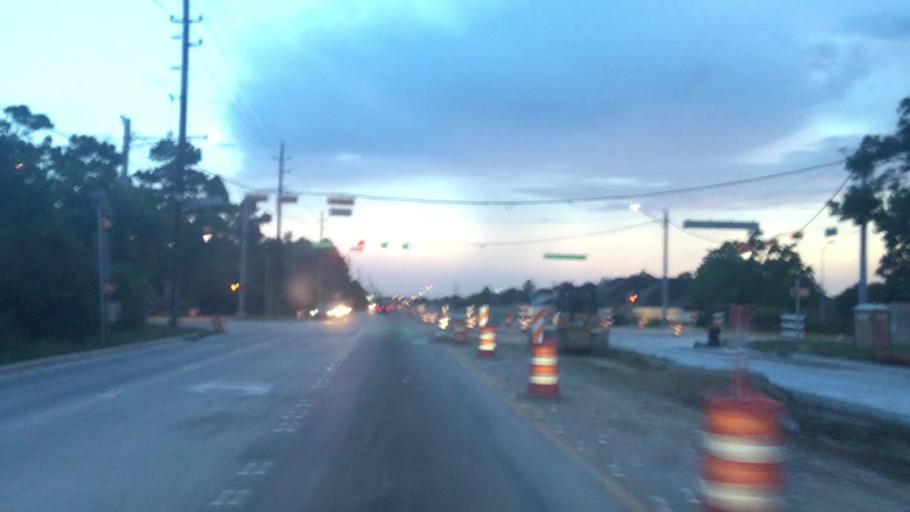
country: US
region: Texas
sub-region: Harris County
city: Humble
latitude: 29.9439
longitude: -95.2497
